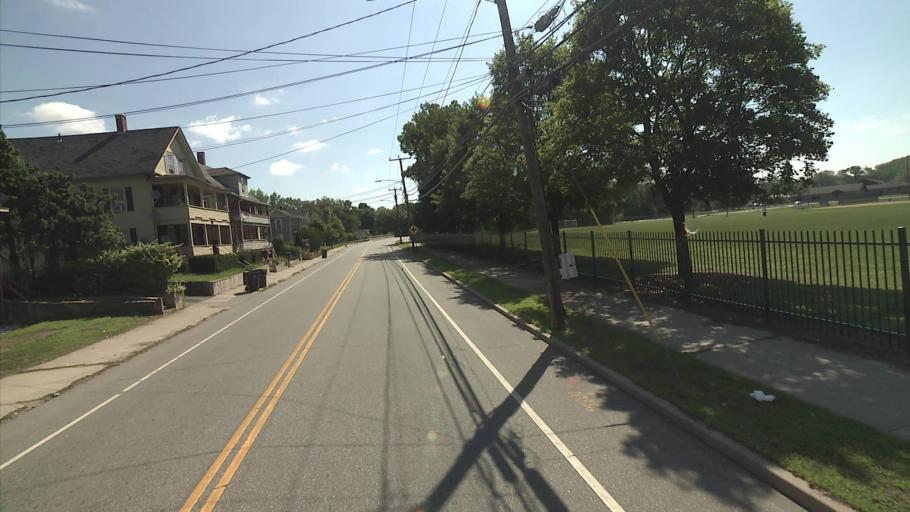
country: US
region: Connecticut
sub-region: Windham County
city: Willimantic
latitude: 41.7158
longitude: -72.1961
